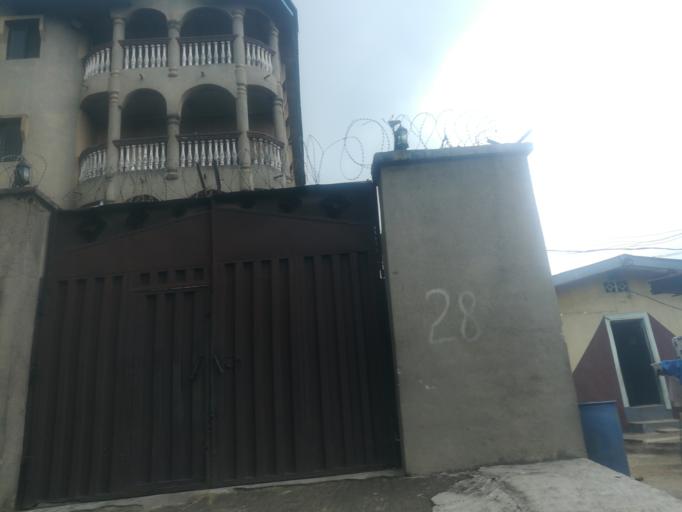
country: NG
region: Lagos
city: Ojota
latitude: 6.5928
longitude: 3.3852
